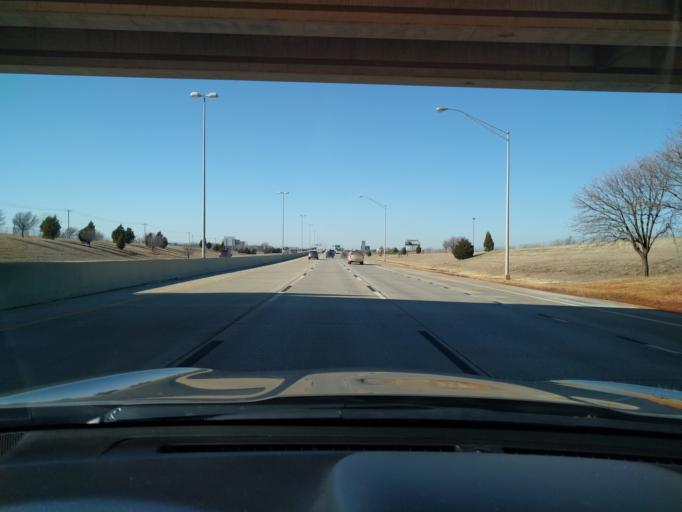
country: US
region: Oklahoma
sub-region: Oklahoma County
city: The Village
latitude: 35.6036
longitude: -97.5214
